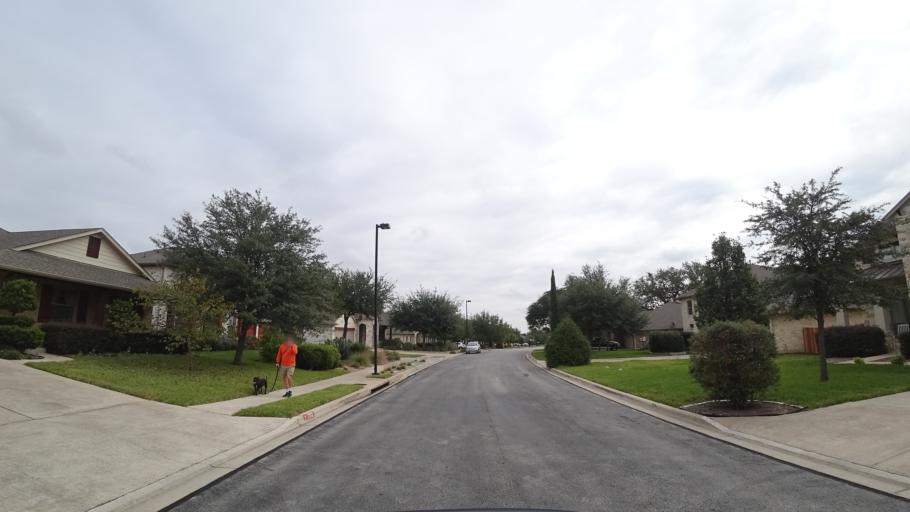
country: US
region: Texas
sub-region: Travis County
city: Shady Hollow
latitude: 30.1970
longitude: -97.9027
